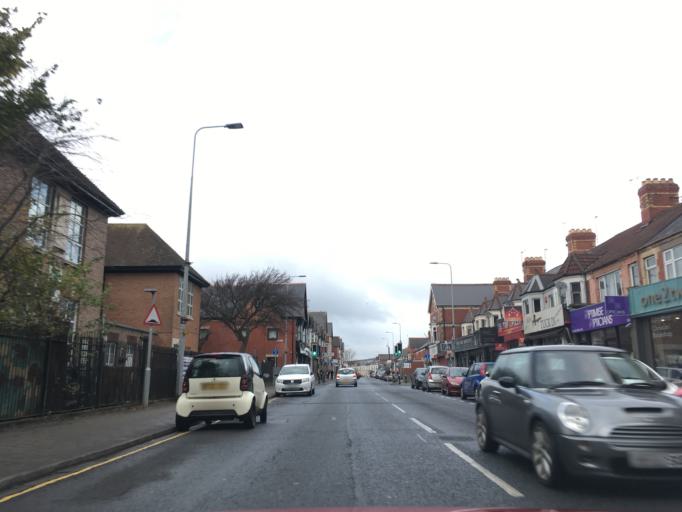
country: GB
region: Wales
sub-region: Cardiff
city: Cardiff
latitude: 51.5013
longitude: -3.1884
